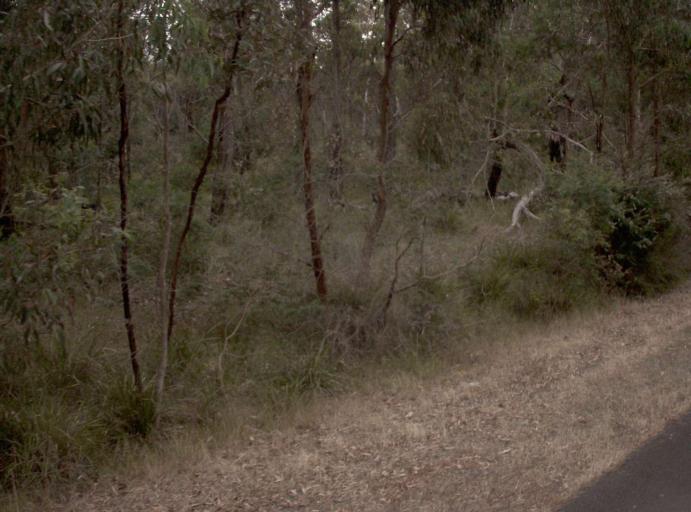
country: AU
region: Victoria
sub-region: Wellington
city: Sale
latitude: -38.4092
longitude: 146.9645
